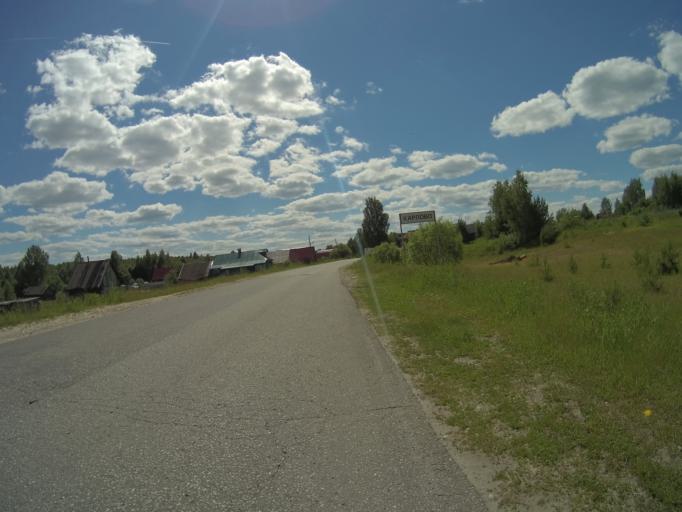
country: RU
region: Vladimir
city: Sudogda
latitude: 56.0806
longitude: 40.7758
